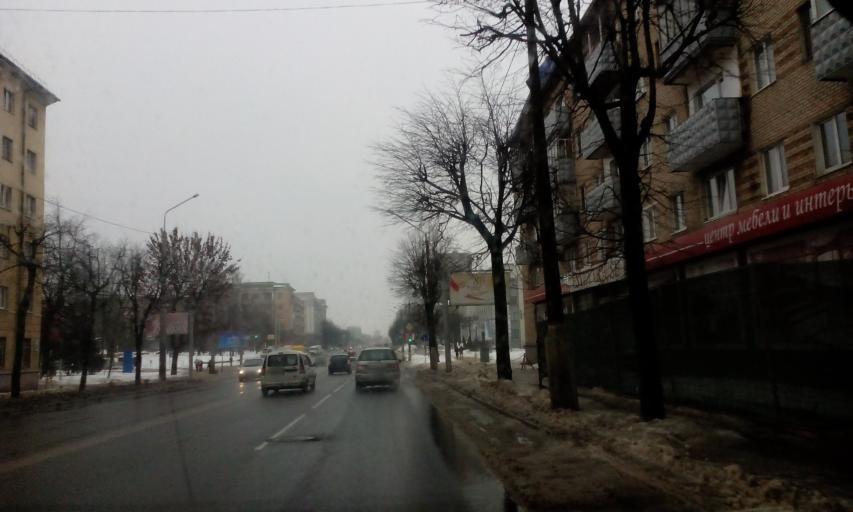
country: BY
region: Mogilev
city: Mahilyow
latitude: 53.9043
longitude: 30.3448
